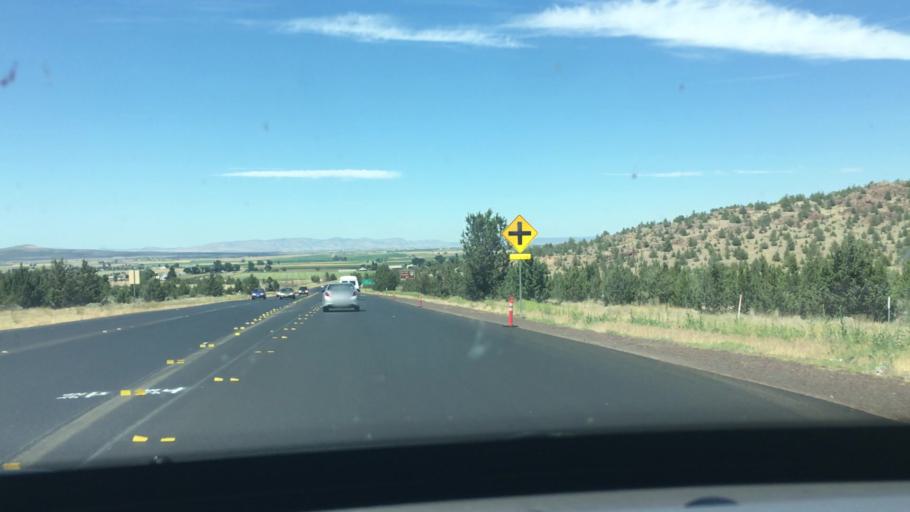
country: US
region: Oregon
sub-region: Jefferson County
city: Culver
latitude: 44.4879
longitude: -121.1934
